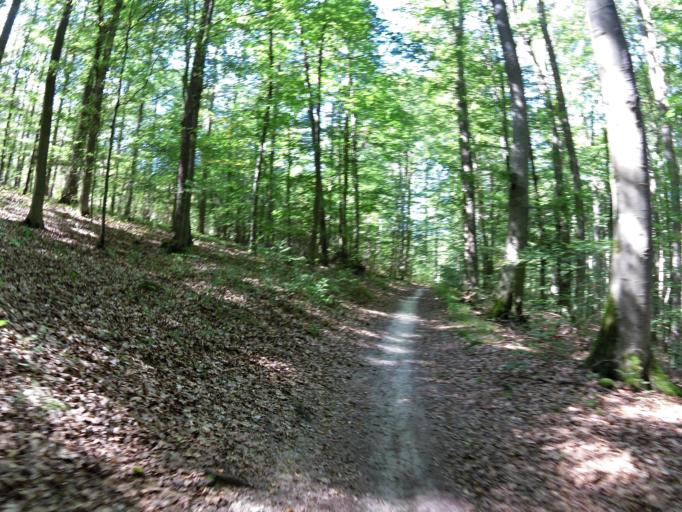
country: DE
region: Bavaria
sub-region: Regierungsbezirk Unterfranken
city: Thungersheim
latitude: 49.8661
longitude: 9.8753
